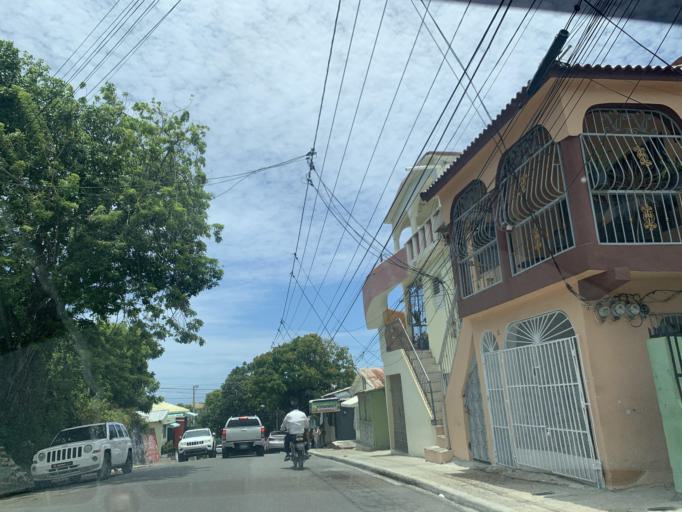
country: DO
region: Puerto Plata
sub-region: Puerto Plata
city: Puerto Plata
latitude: 19.7924
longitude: -70.6838
